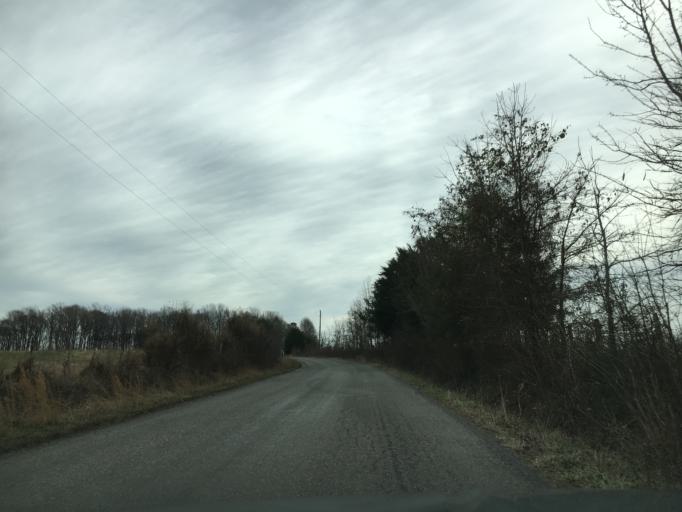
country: US
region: Virginia
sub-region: Amelia County
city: Amelia Court House
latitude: 37.4145
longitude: -77.9827
